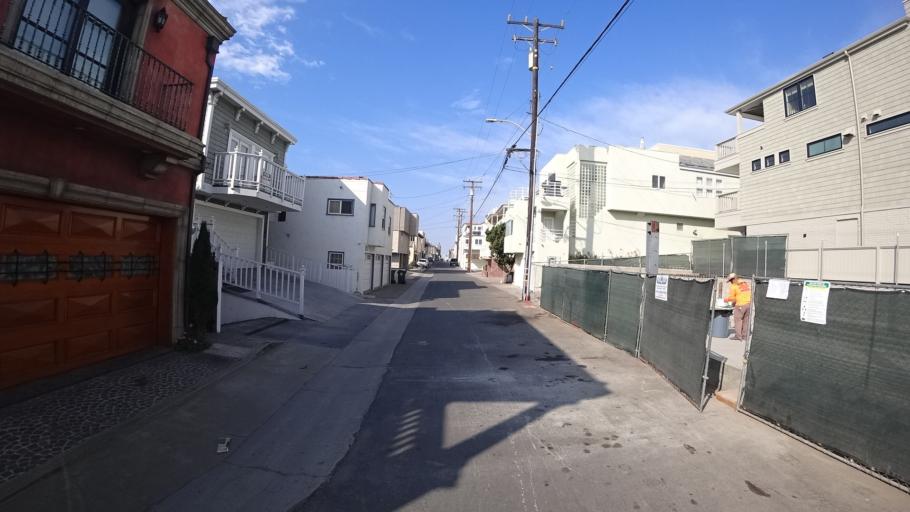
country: US
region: California
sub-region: Los Angeles County
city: Manhattan Beach
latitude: 33.8859
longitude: -118.4121
